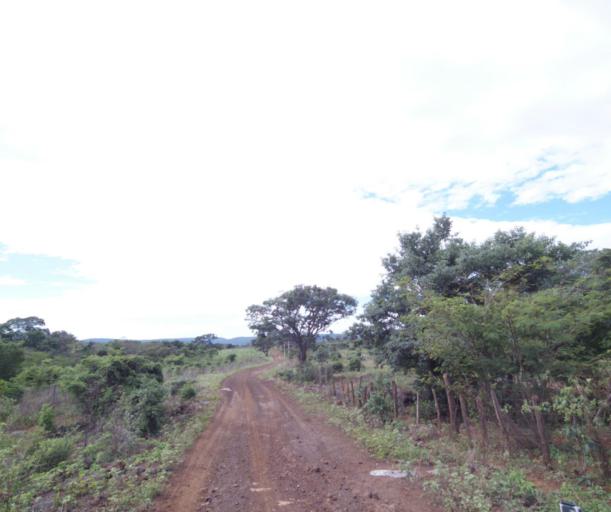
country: BR
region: Bahia
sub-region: Carinhanha
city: Carinhanha
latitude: -14.2439
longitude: -44.4248
